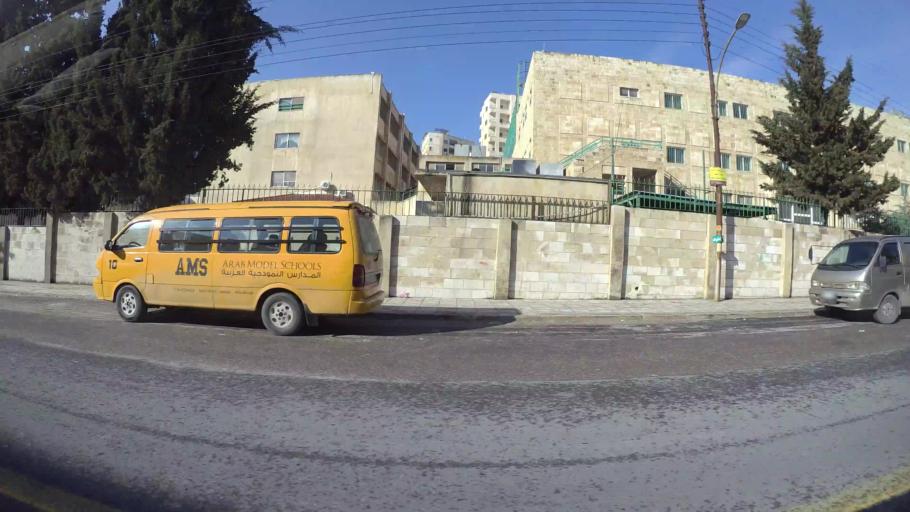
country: JO
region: Amman
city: Al Jubayhah
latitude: 31.9986
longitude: 35.8585
